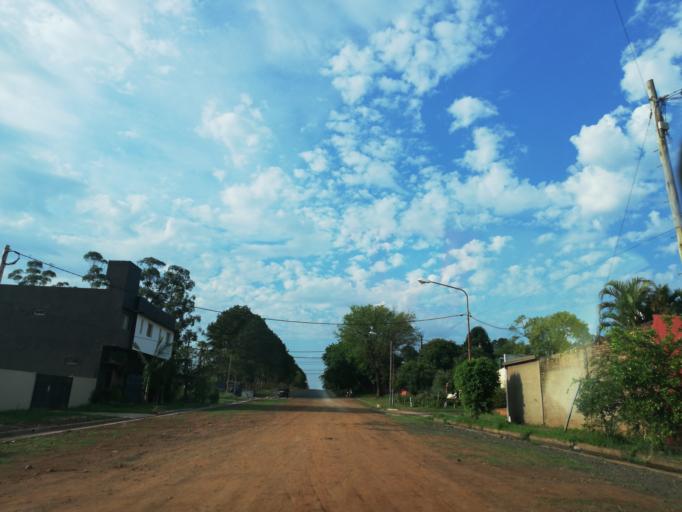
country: AR
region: Misiones
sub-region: Departamento de Capital
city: Posadas
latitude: -27.3657
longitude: -55.9543
